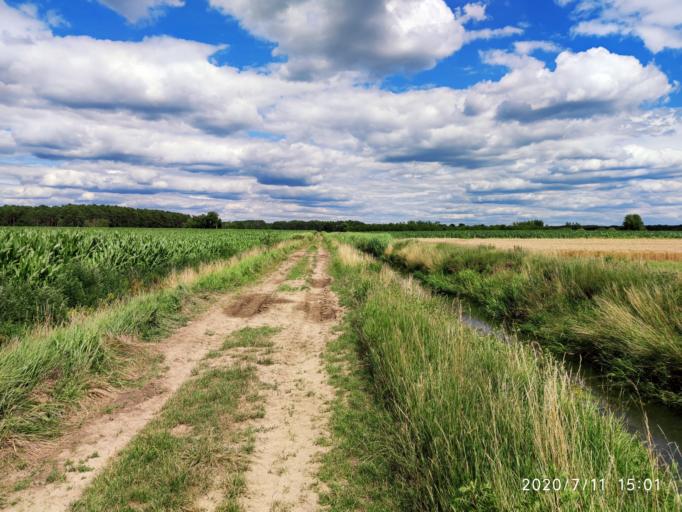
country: PL
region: Lubusz
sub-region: Powiat krosnienski
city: Maszewo
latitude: 52.0444
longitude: 14.9613
